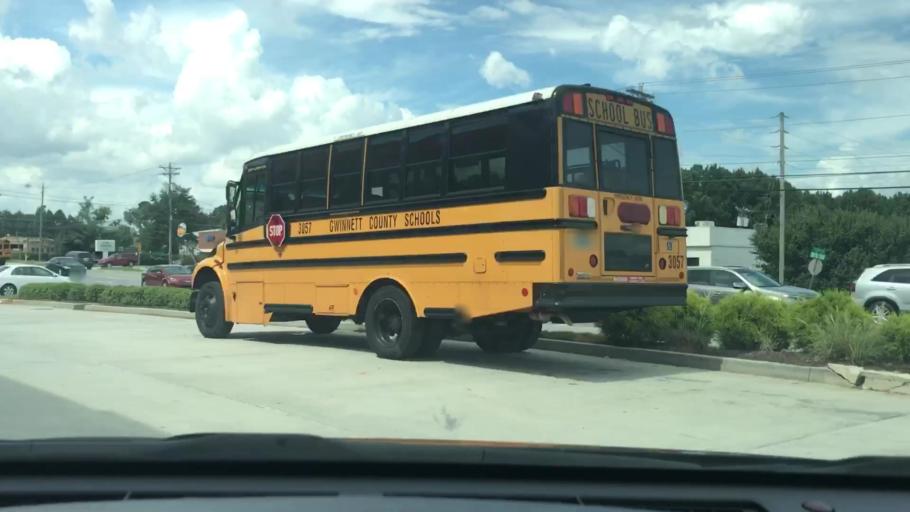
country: US
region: Georgia
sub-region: Gwinnett County
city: Lawrenceville
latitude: 33.9606
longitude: -84.0052
